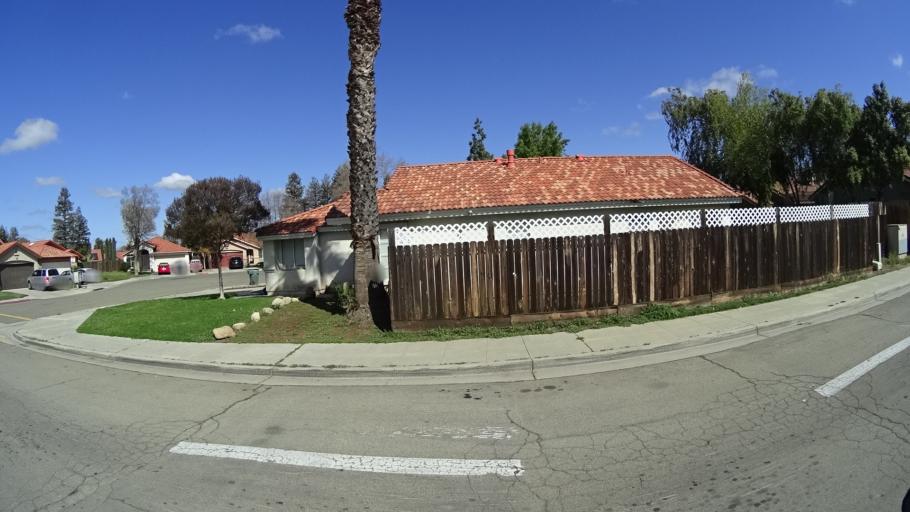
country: US
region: California
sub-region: Fresno County
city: West Park
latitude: 36.8262
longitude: -119.8920
